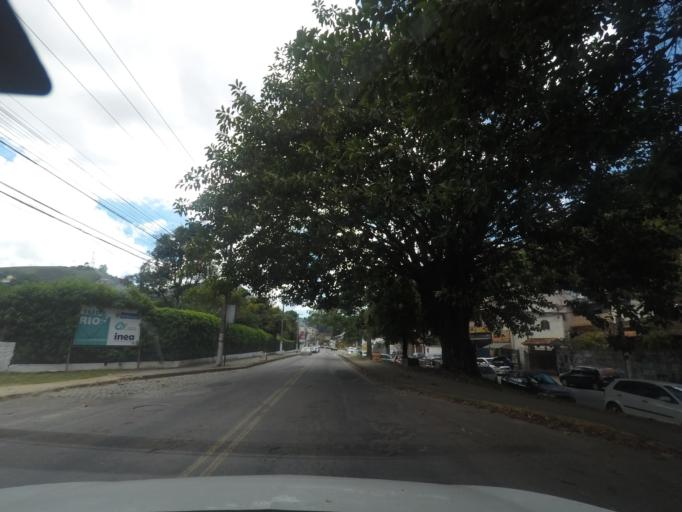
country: BR
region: Rio de Janeiro
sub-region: Teresopolis
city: Teresopolis
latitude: -22.4031
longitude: -42.9693
